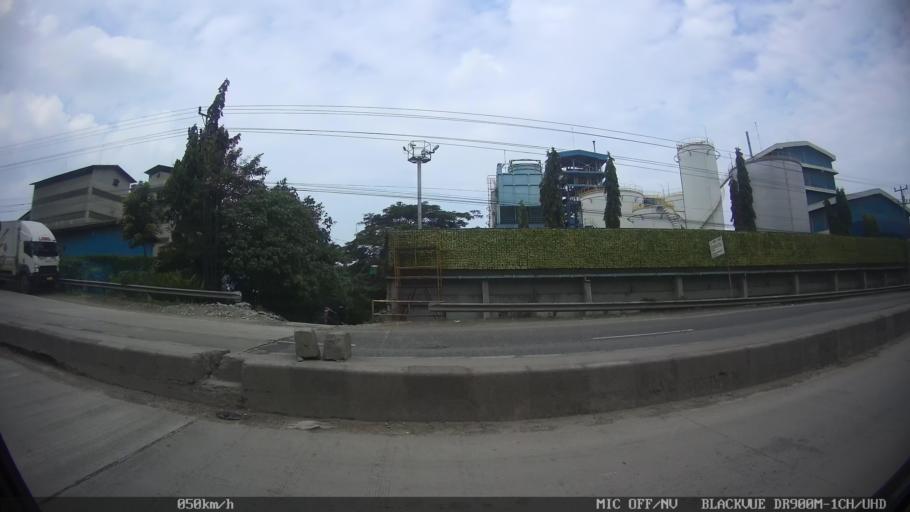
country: ID
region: Lampung
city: Panjang
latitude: -5.4584
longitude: 105.3167
